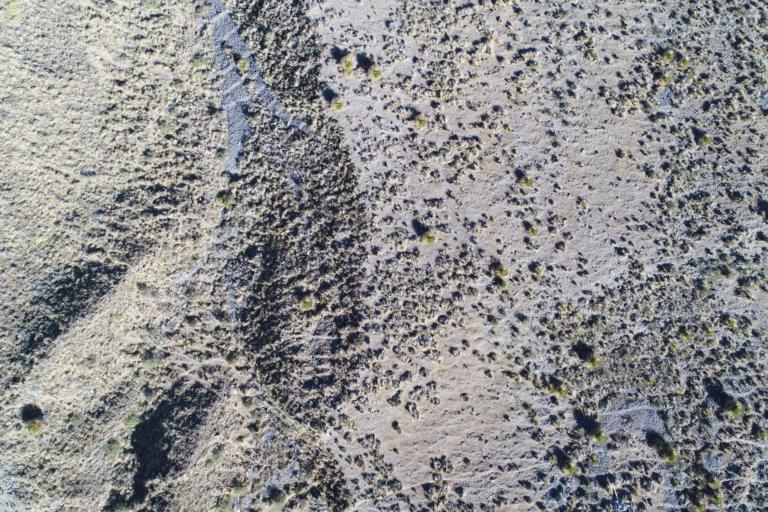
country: BO
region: La Paz
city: Viloco
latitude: -16.8084
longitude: -67.5506
